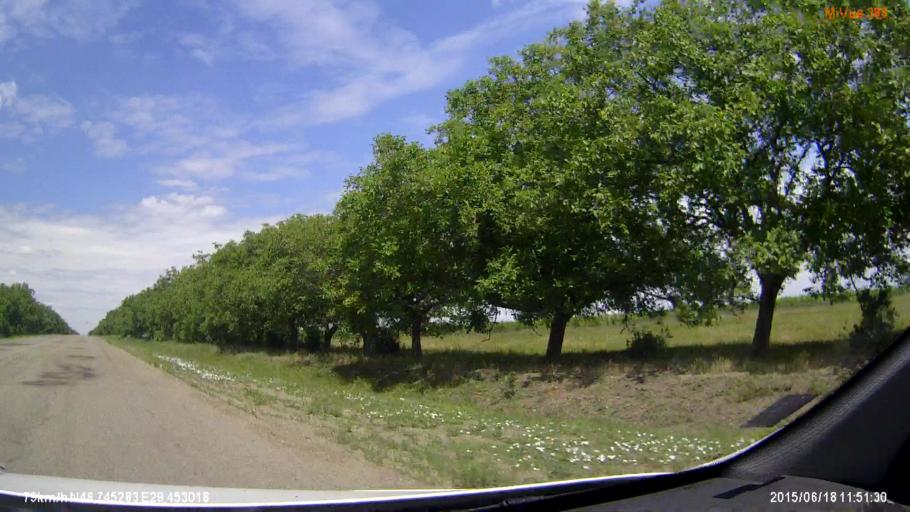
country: MD
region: Bender
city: Bender
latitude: 46.7449
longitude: 29.4529
